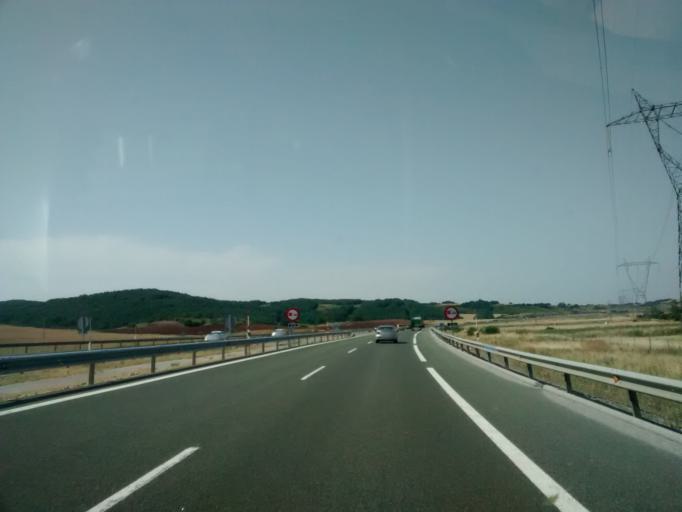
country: ES
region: Cantabria
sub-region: Provincia de Cantabria
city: Mataporquera
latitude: 42.8499
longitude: -4.1697
